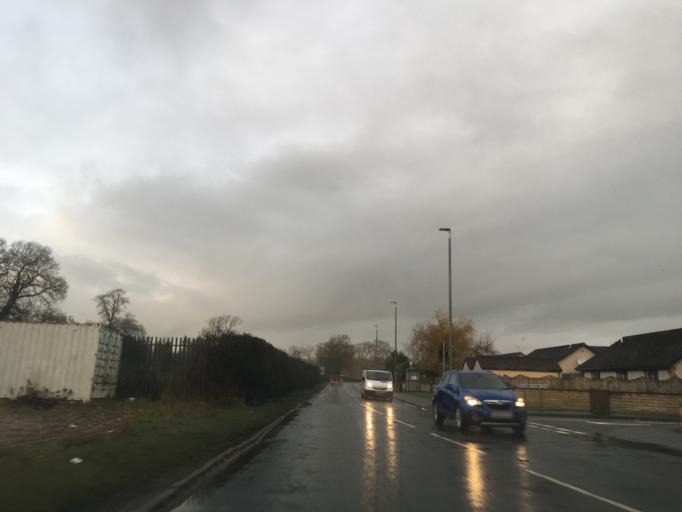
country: GB
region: Scotland
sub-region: Falkirk
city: Airth
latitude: 56.0704
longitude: -3.7738
